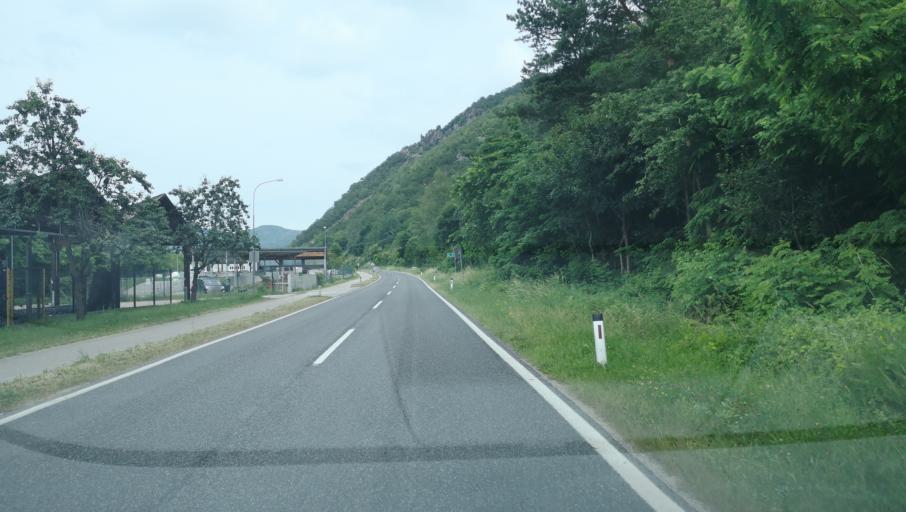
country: AT
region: Lower Austria
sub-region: Politischer Bezirk Krems
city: Weinzierl am Walde
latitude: 48.3831
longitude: 15.4646
